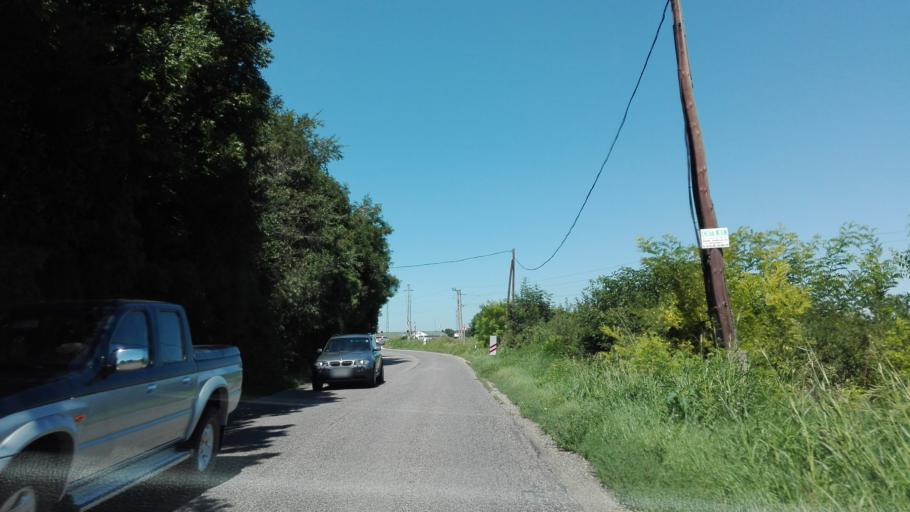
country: HU
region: Fejer
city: Lepseny
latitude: 46.9843
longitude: 18.1938
